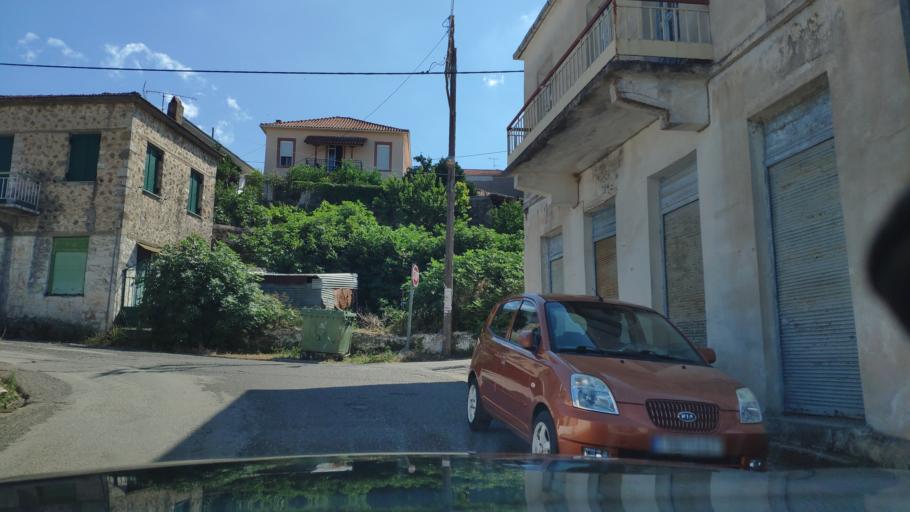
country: GR
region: West Greece
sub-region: Nomos Aitolias kai Akarnanias
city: Katouna
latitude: 38.7868
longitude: 21.1158
